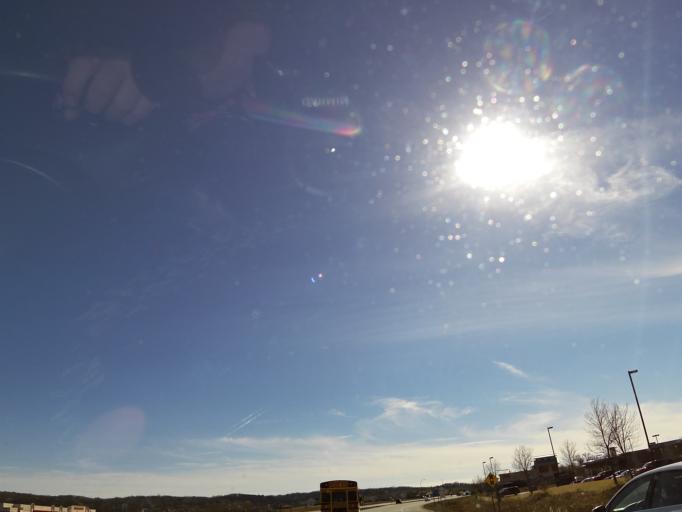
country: US
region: Minnesota
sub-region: Scott County
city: Prior Lake
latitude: 44.7772
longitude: -93.4128
